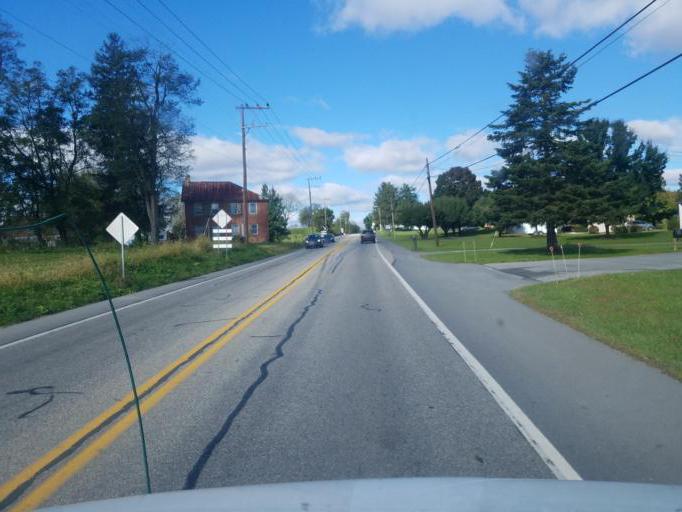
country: US
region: Pennsylvania
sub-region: Franklin County
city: Greencastle
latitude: 39.7923
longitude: -77.7582
